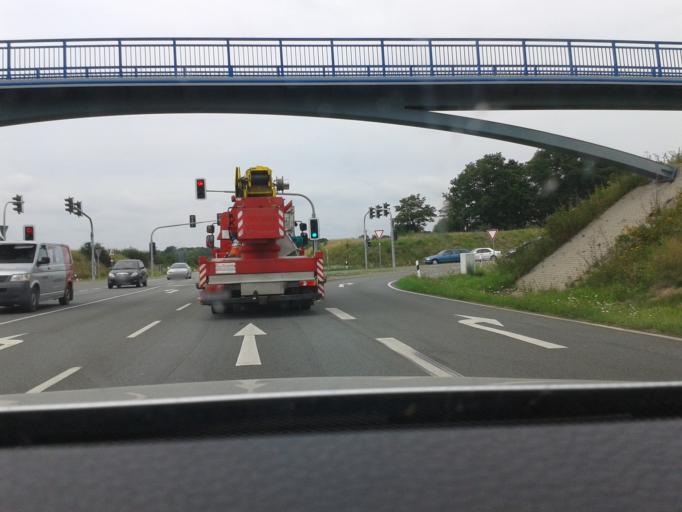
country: DE
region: Lower Saxony
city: Burgdorf
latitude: 52.4555
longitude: 10.0232
